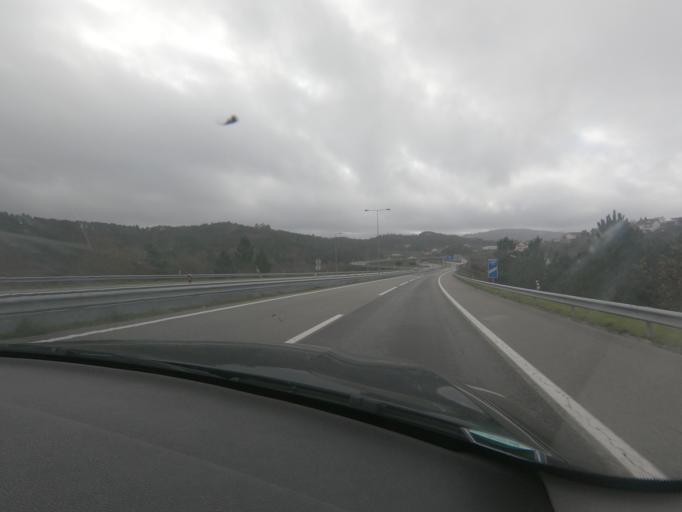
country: PT
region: Viseu
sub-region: Castro Daire
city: Castro Daire
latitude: 40.9057
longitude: -7.9078
